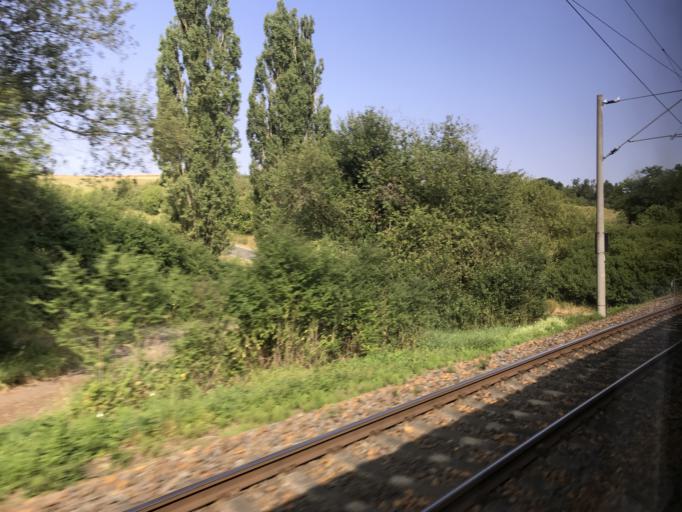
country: DE
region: Hesse
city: Bad Camberg
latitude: 50.3070
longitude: 8.2491
